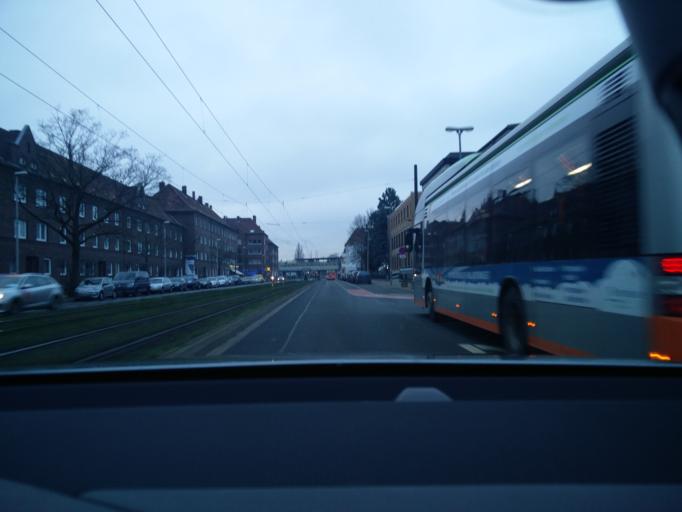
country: DE
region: Lower Saxony
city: Hannover
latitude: 52.3503
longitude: 9.7231
